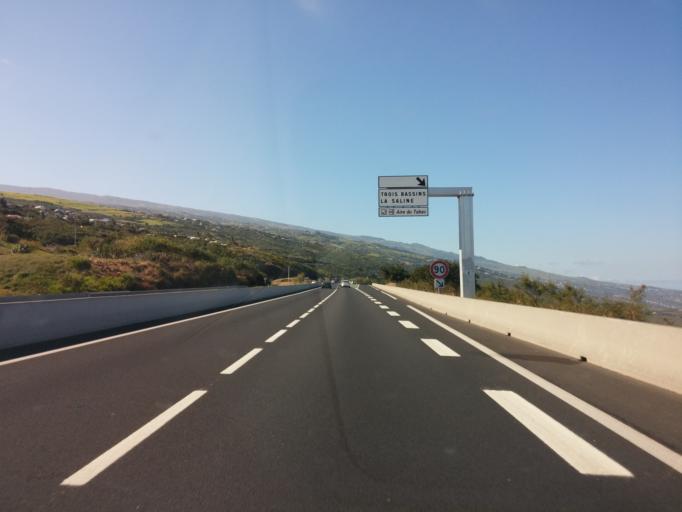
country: RE
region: Reunion
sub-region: Reunion
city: Trois-Bassins
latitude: -21.0986
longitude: 55.2647
